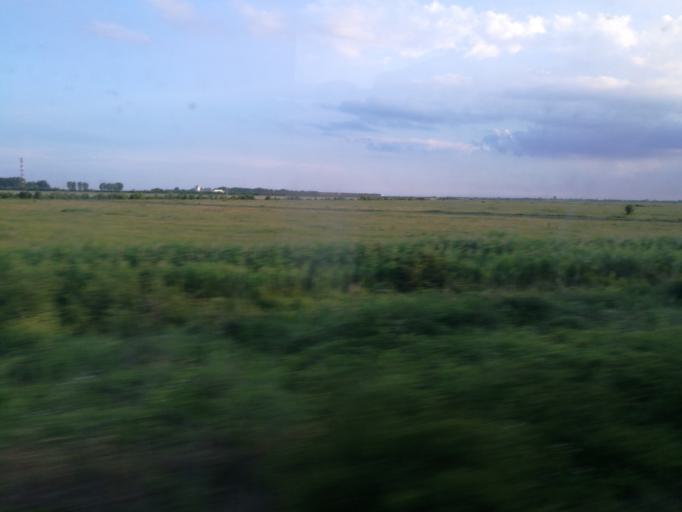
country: RO
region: Dambovita
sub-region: Comuna Contesti
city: Contesti
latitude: 44.6600
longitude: 25.6200
